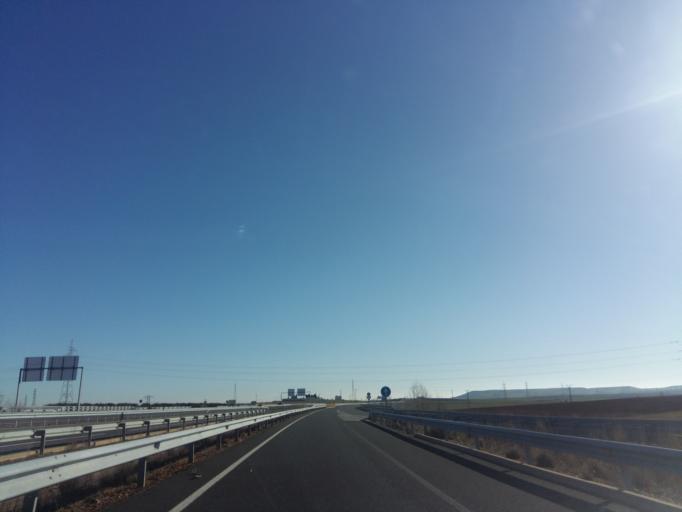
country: ES
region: Castille and Leon
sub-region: Provincia de Palencia
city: Abia de las Torres
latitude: 42.4043
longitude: -4.3846
